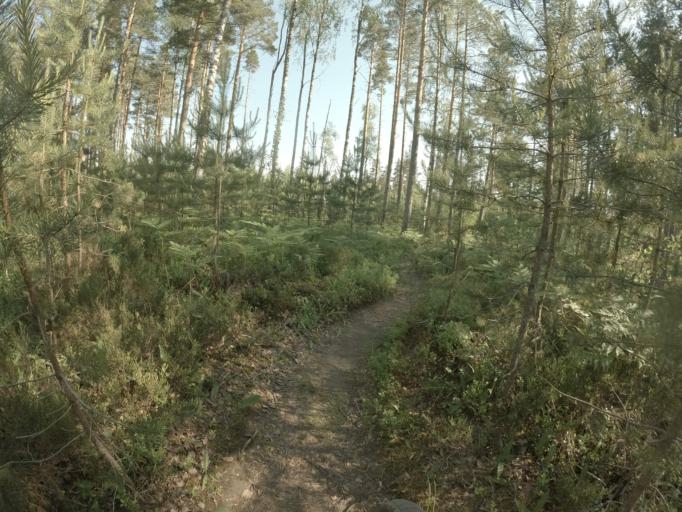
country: RU
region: Leningrad
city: Yakovlevo
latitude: 60.4382
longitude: 29.2389
